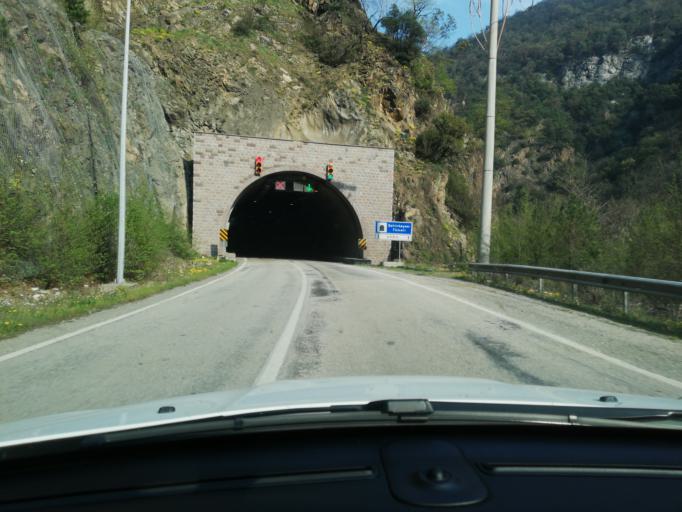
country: TR
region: Karabuk
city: Yenice
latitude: 41.1608
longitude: 32.4587
